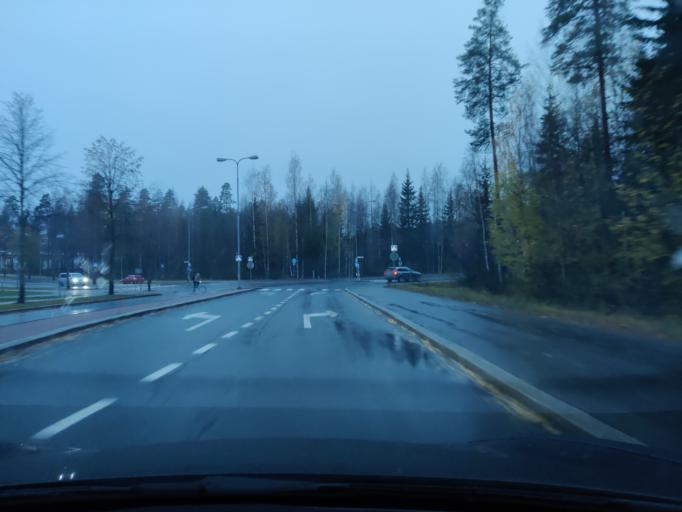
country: FI
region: Northern Savo
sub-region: Kuopio
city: Kuopio
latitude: 62.8306
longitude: 27.6688
